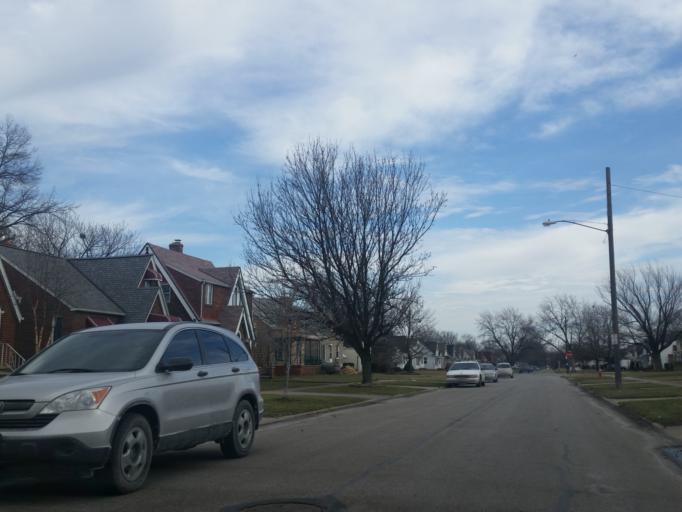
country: US
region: Ohio
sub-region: Cuyahoga County
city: Brooklyn Heights
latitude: 41.4150
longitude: -81.7037
